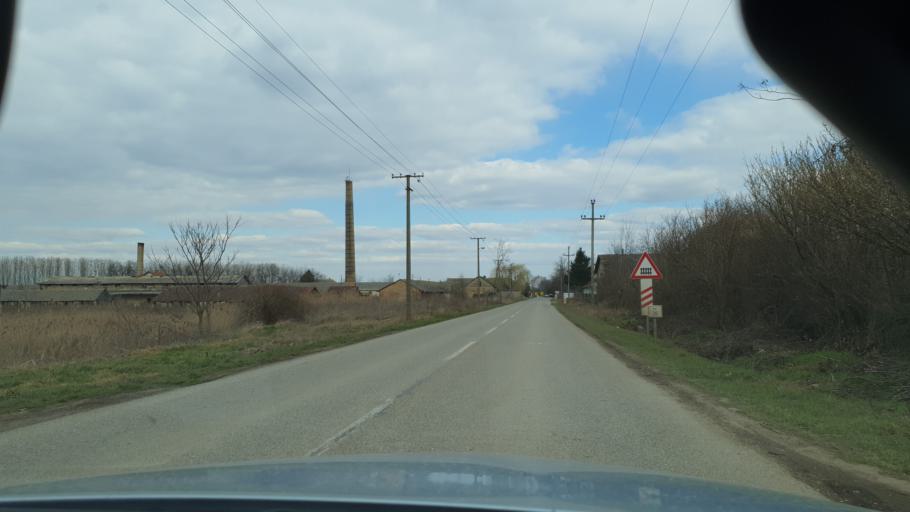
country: RS
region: Autonomna Pokrajina Vojvodina
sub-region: Zapadnobacki Okrug
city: Odzaci
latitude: 45.4461
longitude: 19.3255
